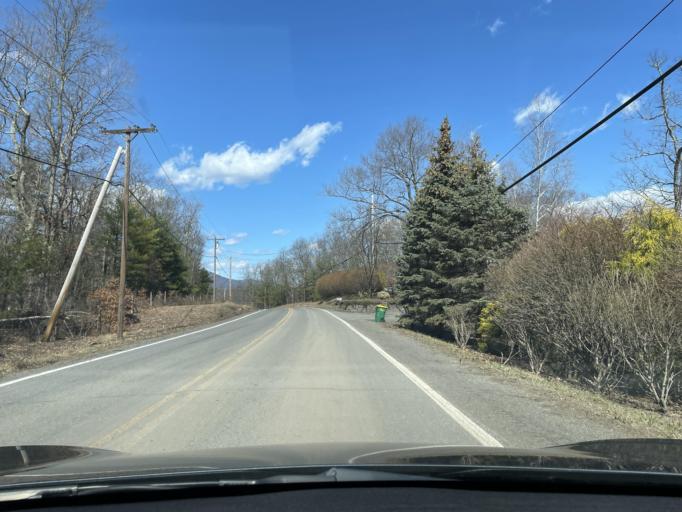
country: US
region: New York
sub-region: Ulster County
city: West Hurley
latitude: 41.9891
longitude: -74.0889
